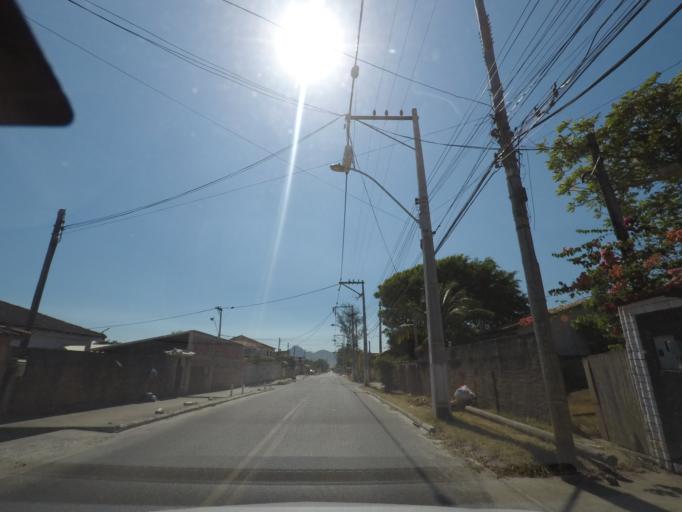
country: BR
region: Rio de Janeiro
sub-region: Marica
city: Marica
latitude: -22.9671
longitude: -42.9564
